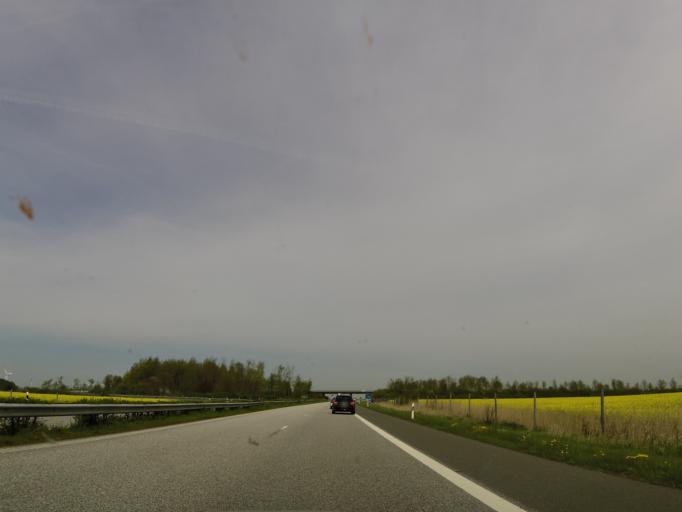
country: DE
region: Schleswig-Holstein
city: Lohe-Rickelshof
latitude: 54.1863
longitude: 9.0489
